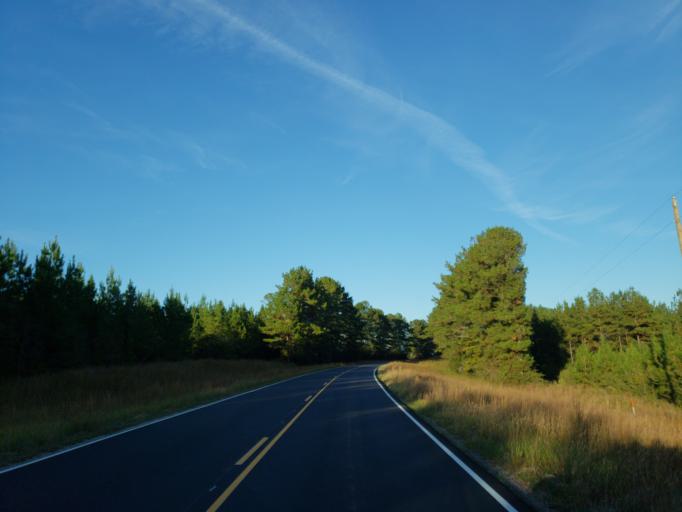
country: US
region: Mississippi
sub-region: Wayne County
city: Belmont
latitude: 31.4235
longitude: -88.5714
